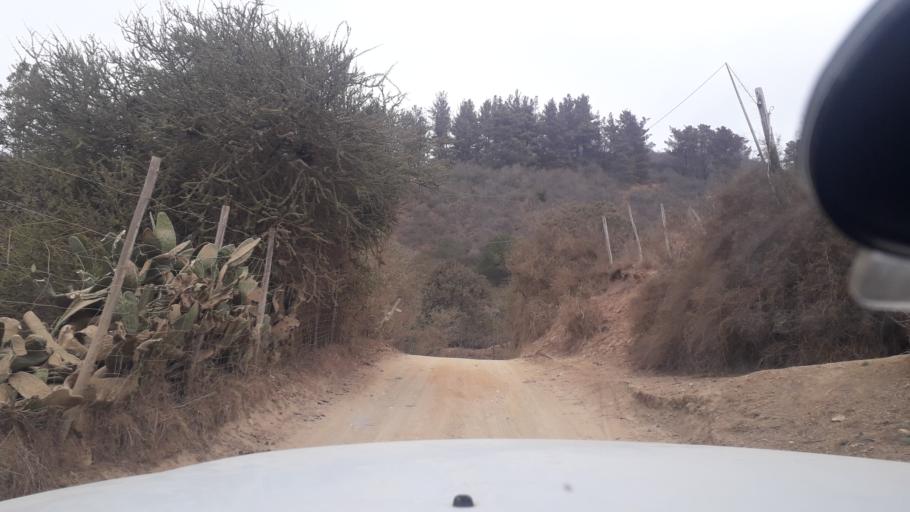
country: CL
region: Valparaiso
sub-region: Provincia de Valparaiso
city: Valparaiso
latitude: -33.1158
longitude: -71.6510
